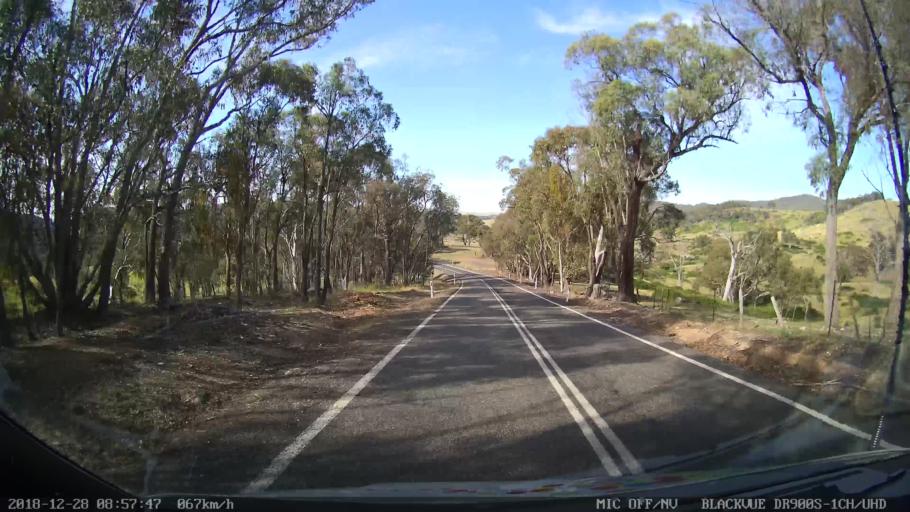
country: AU
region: New South Wales
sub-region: Upper Lachlan Shire
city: Crookwell
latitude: -34.1213
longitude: 149.3329
